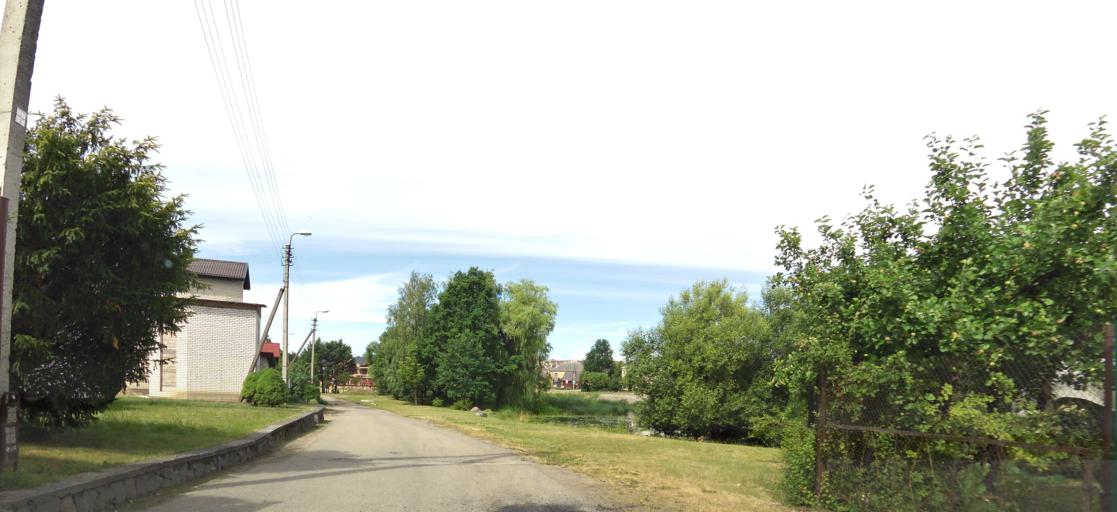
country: LT
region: Panevezys
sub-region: Birzai
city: Birzai
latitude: 56.2031
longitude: 24.7659
